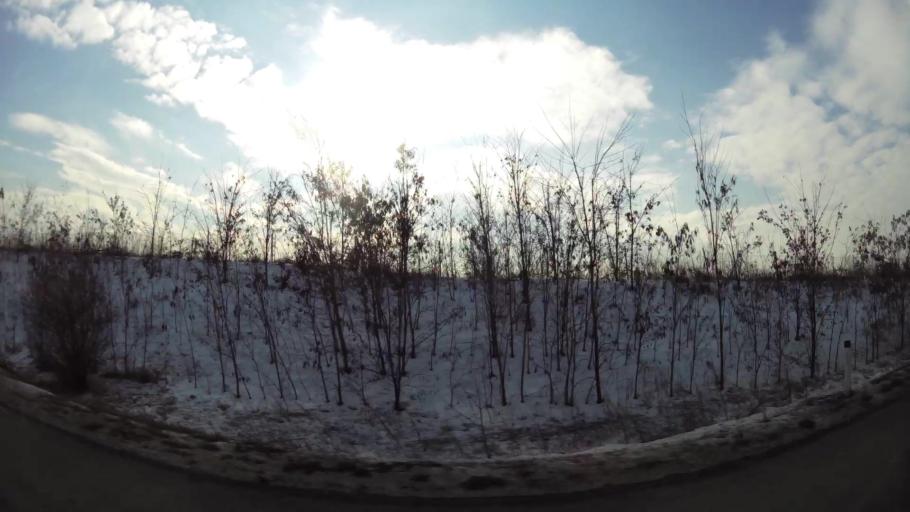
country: MK
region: Suto Orizari
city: Suto Orizare
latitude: 42.0491
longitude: 21.4334
